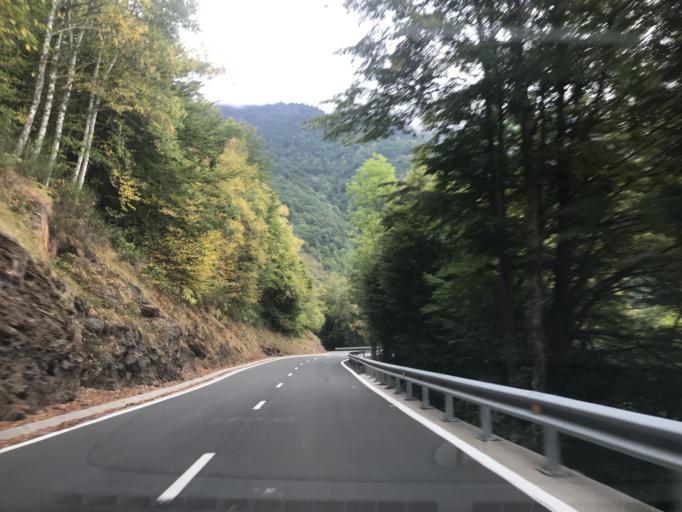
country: ES
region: Catalonia
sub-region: Provincia de Lleida
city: Les
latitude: 42.7797
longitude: 0.6796
